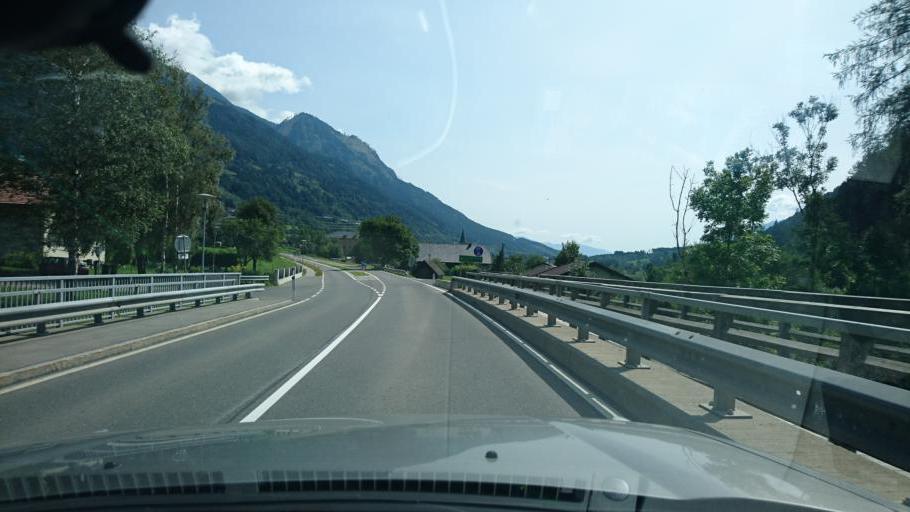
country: AT
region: Carinthia
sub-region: Politischer Bezirk Spittal an der Drau
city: Muhldorf
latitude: 46.8767
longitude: 13.2995
